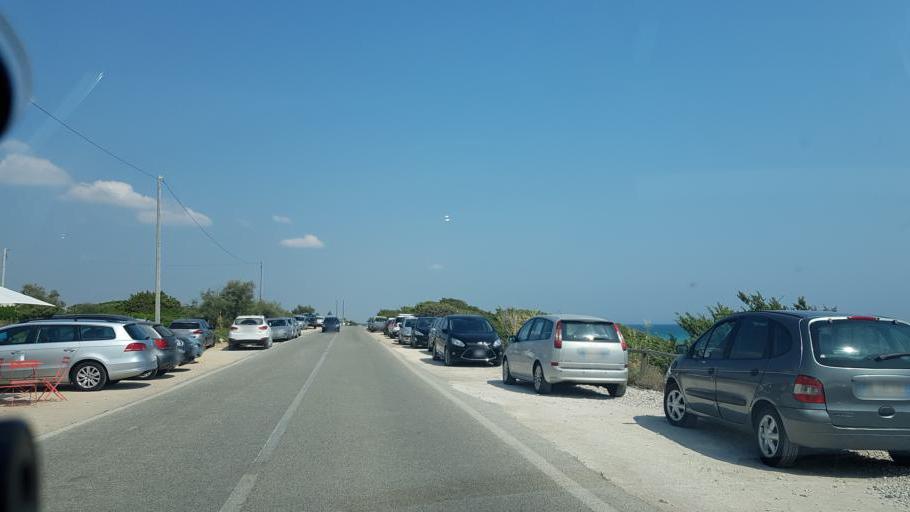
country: IT
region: Apulia
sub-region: Provincia di Taranto
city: Maruggio
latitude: 40.3016
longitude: 17.6148
